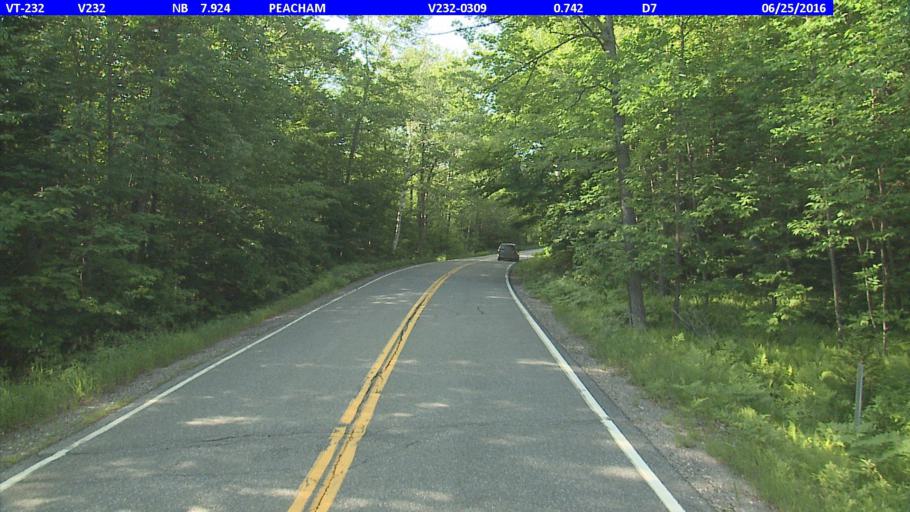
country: US
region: Vermont
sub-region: Caledonia County
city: Hardwick
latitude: 44.3061
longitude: -72.3033
